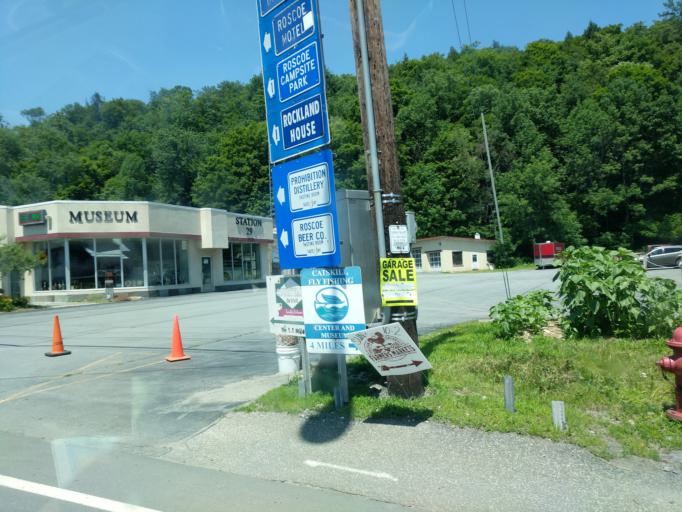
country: US
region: New York
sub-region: Sullivan County
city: Livingston Manor
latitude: 41.9328
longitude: -74.9128
